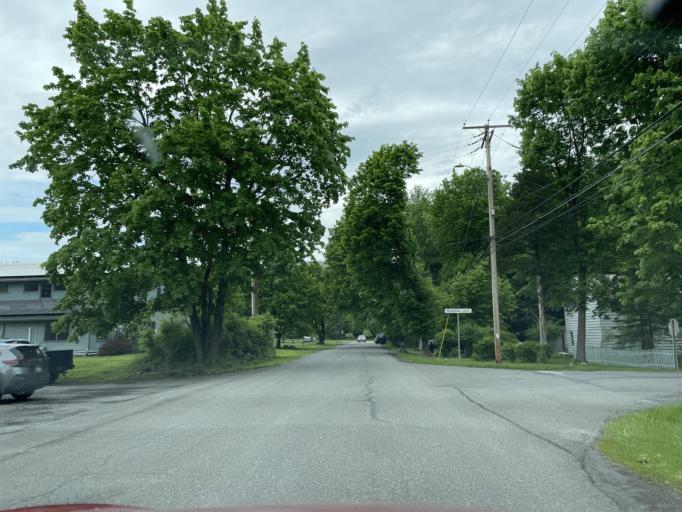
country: US
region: New York
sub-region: Ulster County
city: Woodstock
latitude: 42.0390
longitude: -74.1468
